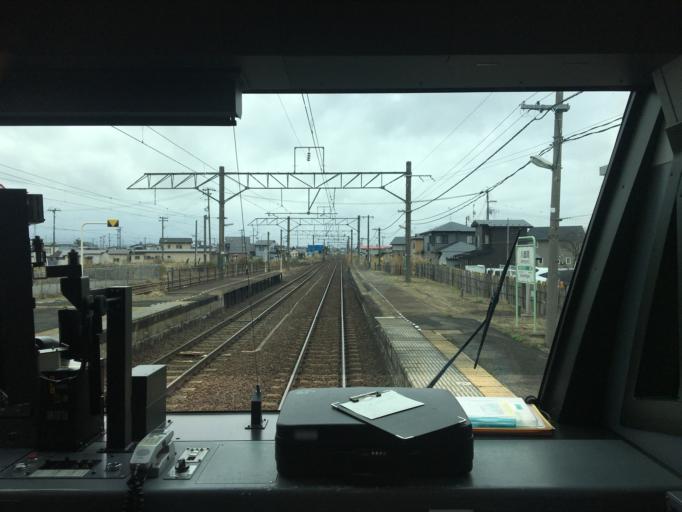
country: JP
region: Akita
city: Tenno
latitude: 39.9472
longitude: 140.0787
